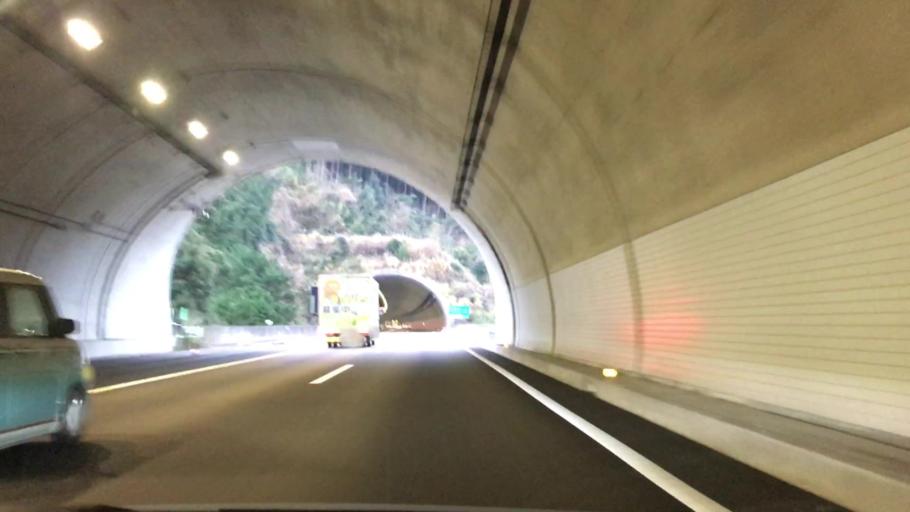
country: JP
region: Shizuoka
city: Shimada
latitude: 34.8699
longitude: 138.1645
